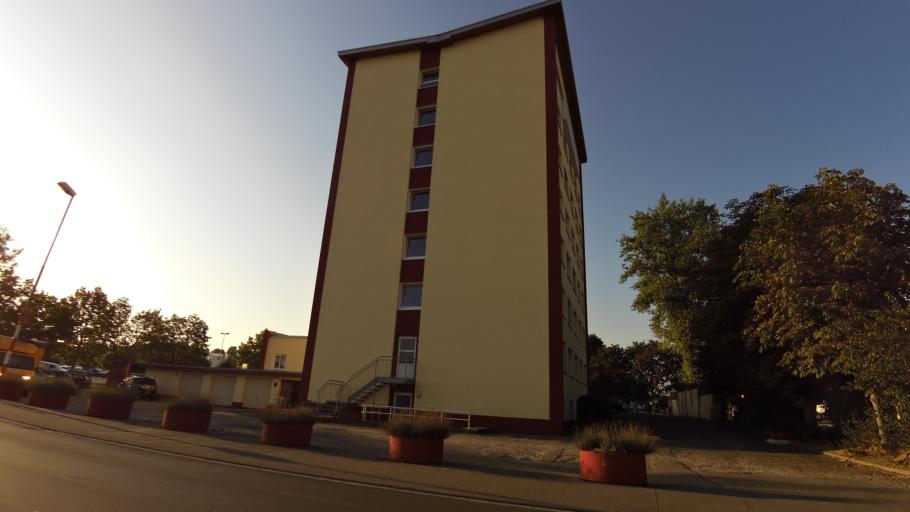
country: DE
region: Baden-Wuerttemberg
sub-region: Freiburg Region
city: Kehl
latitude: 48.5770
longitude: 7.8154
